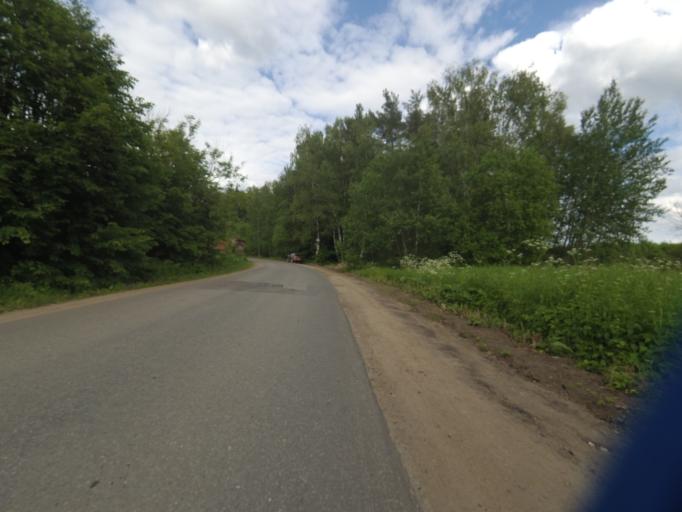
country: RU
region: Moskovskaya
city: Marfino
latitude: 56.0913
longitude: 37.5634
